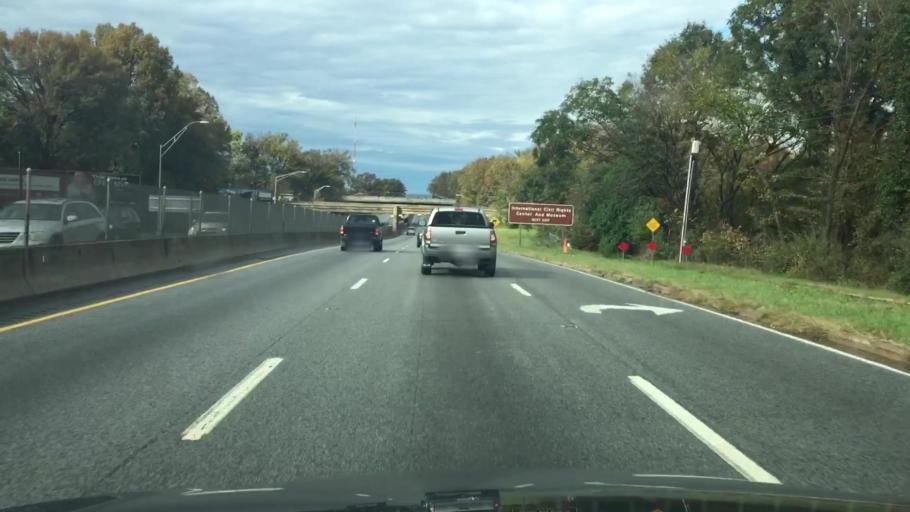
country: US
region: North Carolina
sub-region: Guilford County
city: Greensboro
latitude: 36.0709
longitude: -79.7661
